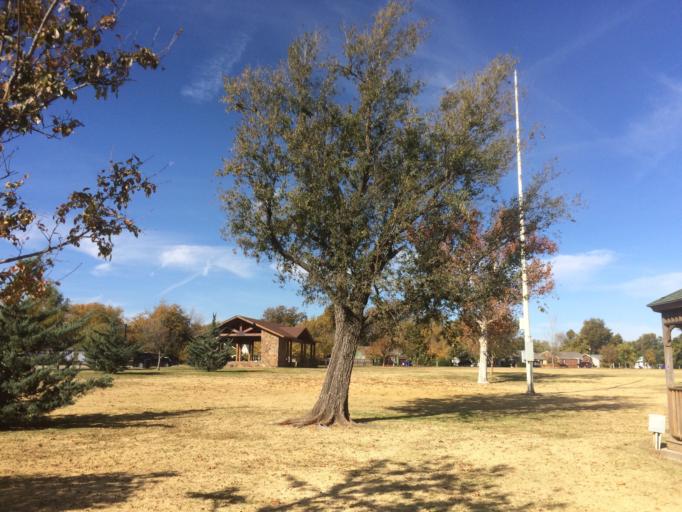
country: US
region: Oklahoma
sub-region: Cleveland County
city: Norman
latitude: 35.2238
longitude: -97.4480
